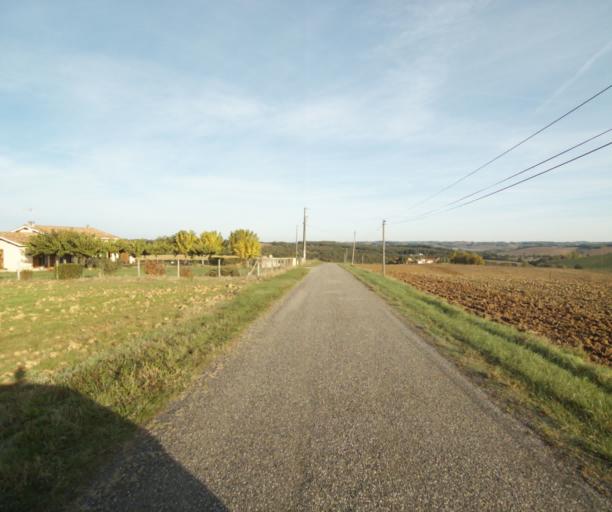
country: FR
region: Midi-Pyrenees
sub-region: Departement du Tarn-et-Garonne
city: Nohic
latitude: 43.9187
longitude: 1.4811
